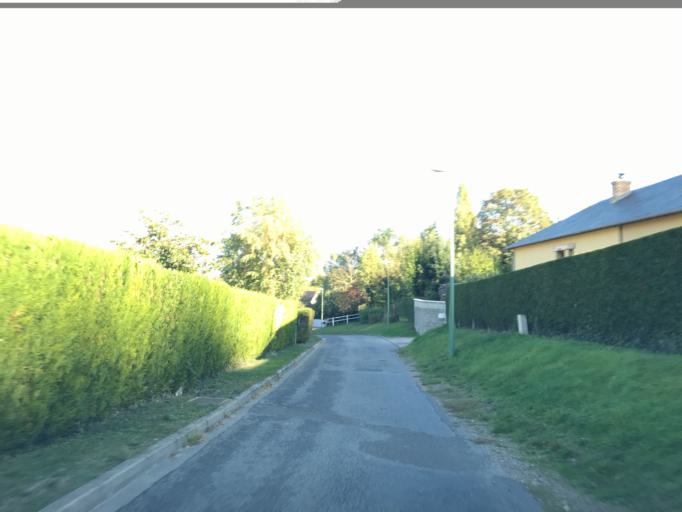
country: FR
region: Haute-Normandie
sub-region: Departement de l'Eure
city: Houlbec-Cocherel
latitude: 49.0722
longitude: 1.2799
